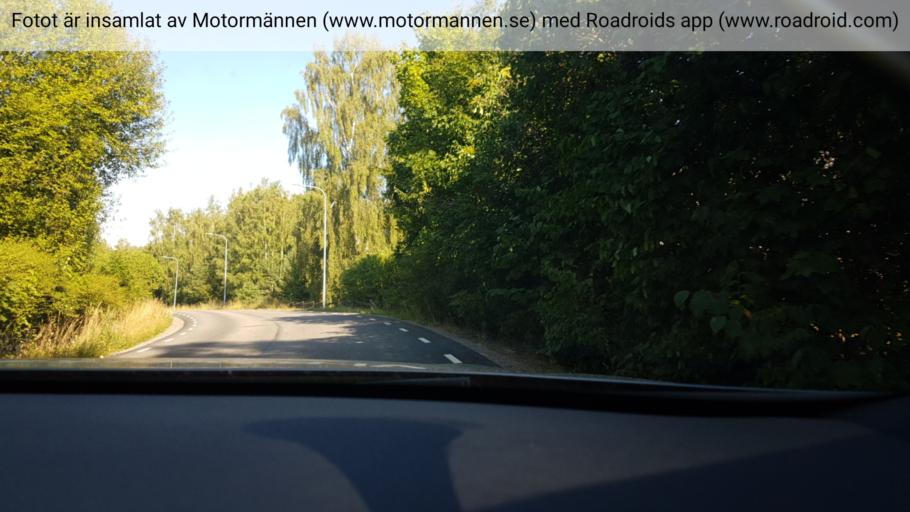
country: SE
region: Vaestra Goetaland
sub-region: Mariestads Kommun
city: Mariestad
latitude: 58.6406
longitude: 13.6861
